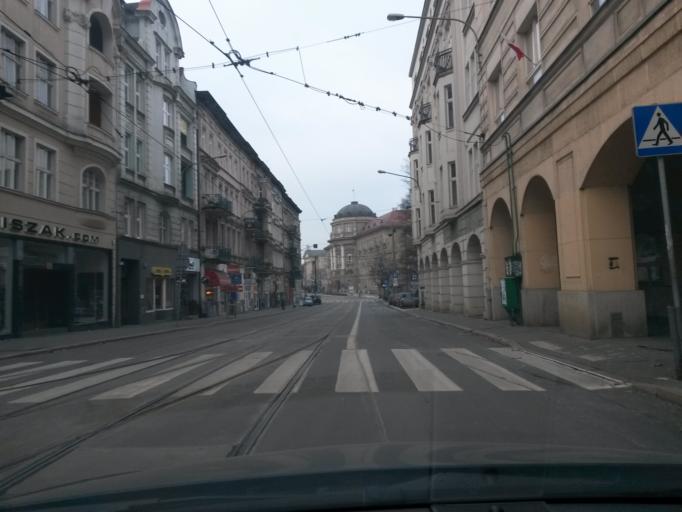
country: PL
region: Greater Poland Voivodeship
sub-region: Poznan
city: Poznan
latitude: 52.4086
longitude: 16.9216
